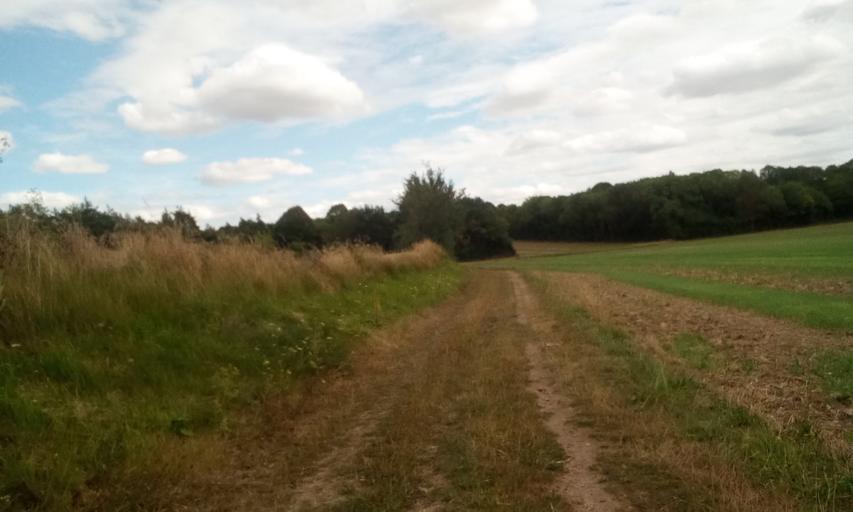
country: FR
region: Lower Normandy
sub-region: Departement du Calvados
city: Bellengreville
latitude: 49.1143
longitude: -0.1989
